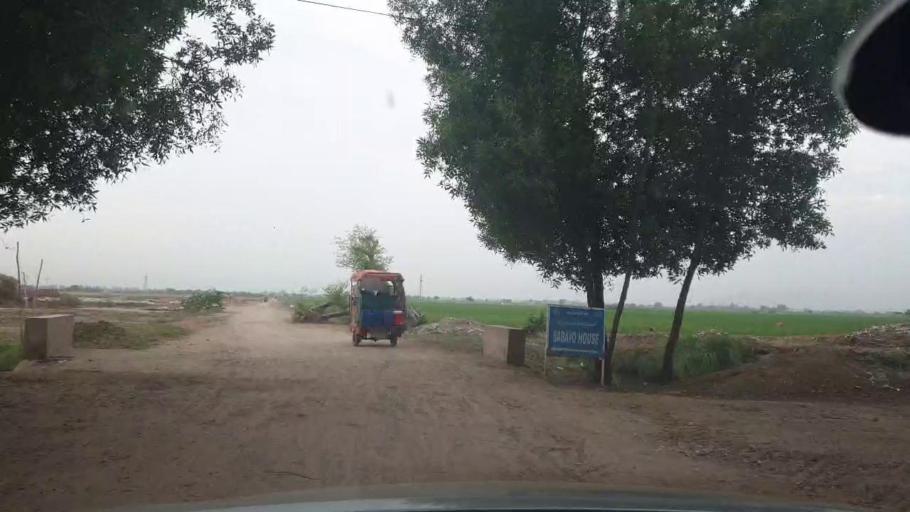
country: PK
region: Sindh
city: Jacobabad
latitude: 28.2893
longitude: 68.4180
